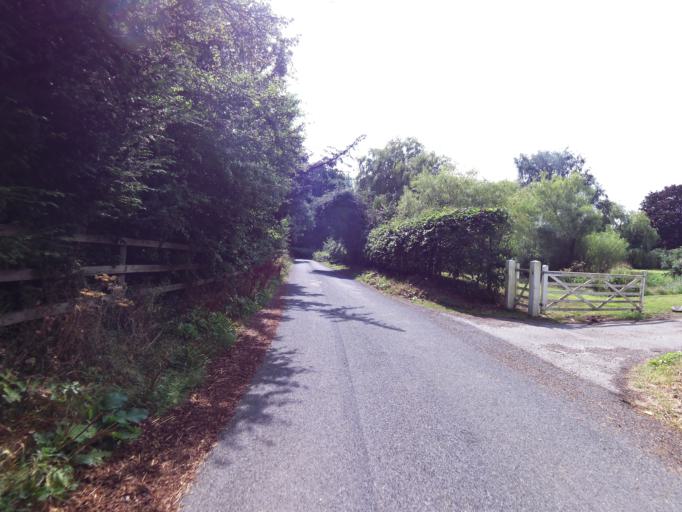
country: GB
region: England
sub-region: Hertfordshire
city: Shenley AV
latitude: 51.6961
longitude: -0.2551
